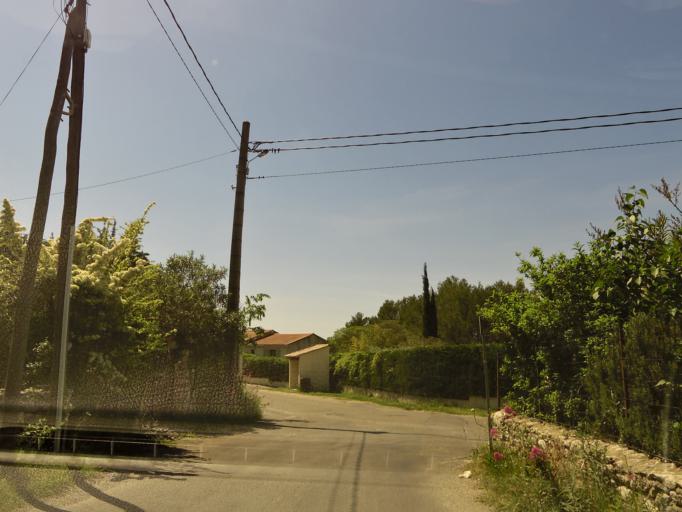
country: FR
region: Languedoc-Roussillon
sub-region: Departement du Gard
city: Villevieille
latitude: 43.7915
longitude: 4.0992
